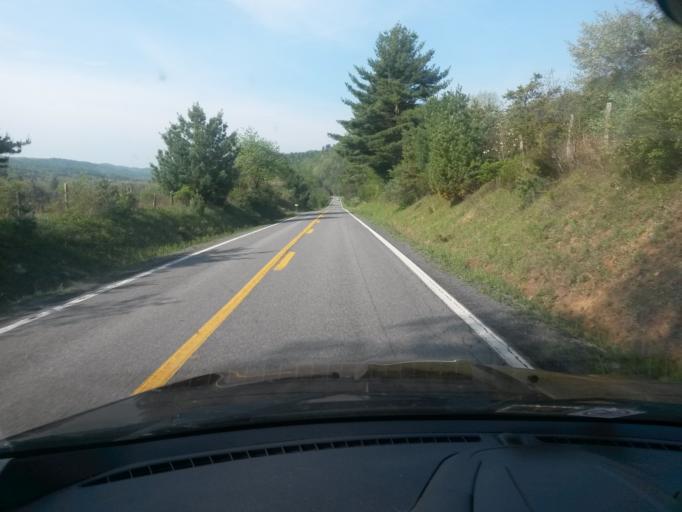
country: US
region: West Virginia
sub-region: Pocahontas County
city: Marlinton
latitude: 38.0337
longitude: -80.0357
